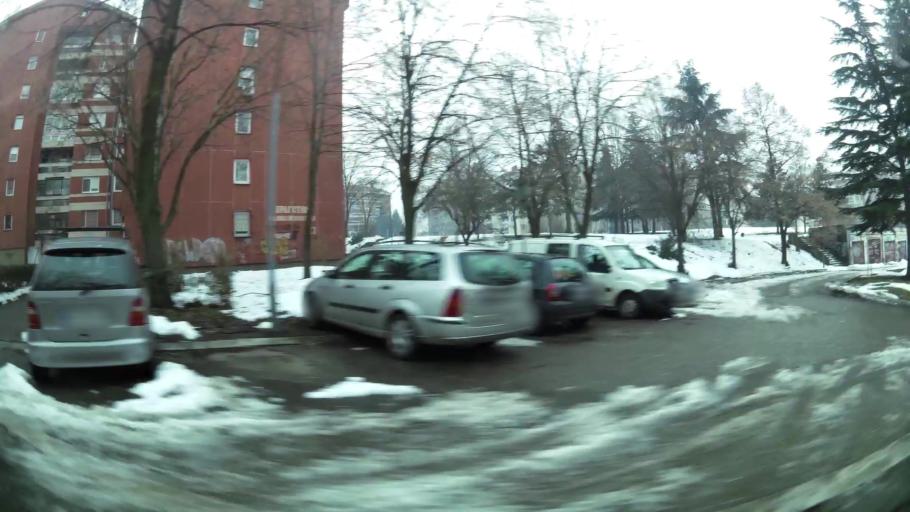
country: RS
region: Central Serbia
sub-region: Belgrade
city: Vozdovac
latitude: 44.7710
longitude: 20.5003
